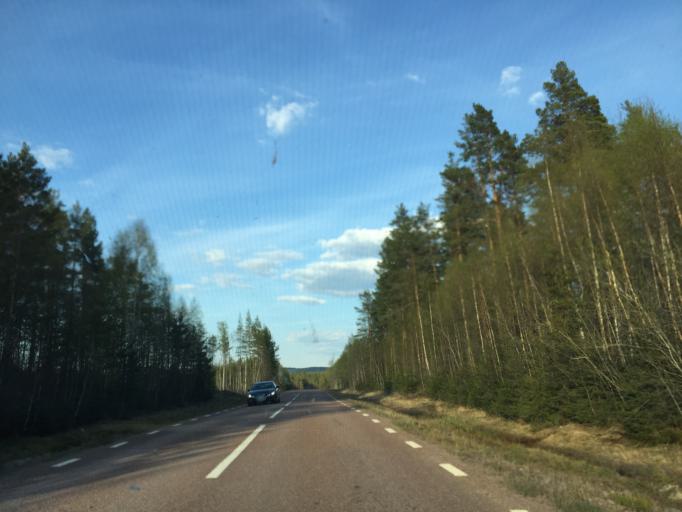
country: SE
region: Dalarna
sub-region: Leksand Municipality
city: Siljansnas
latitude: 60.6758
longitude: 14.6900
